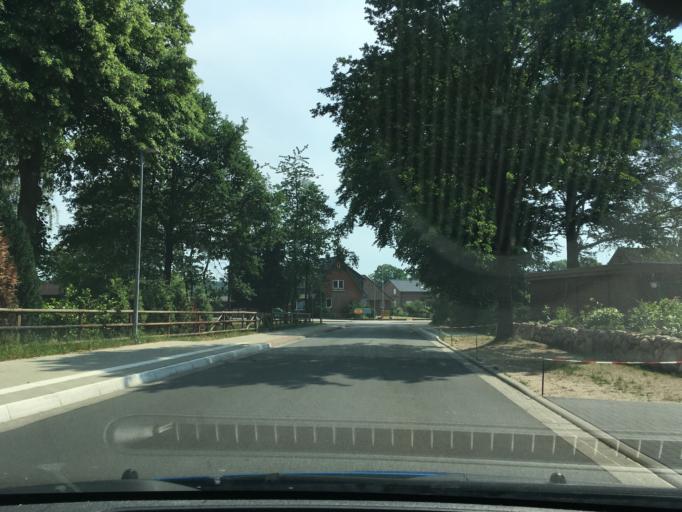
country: DE
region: Lower Saxony
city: Jesteburg
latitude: 53.2727
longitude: 9.9151
